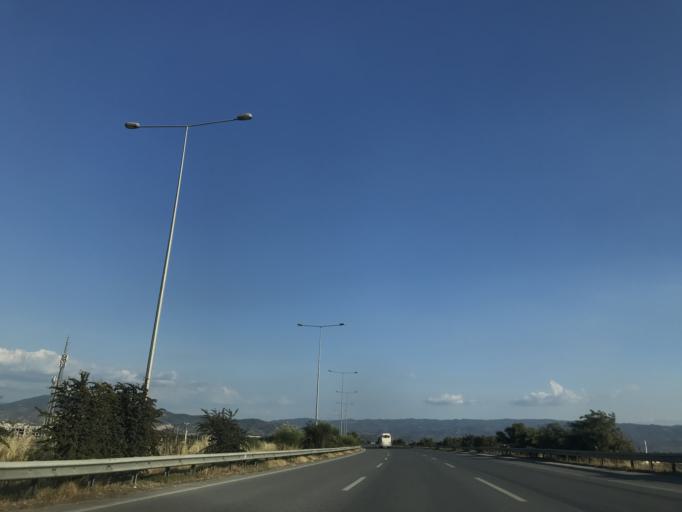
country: TR
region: Aydin
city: Aydin
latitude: 37.8309
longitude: 27.8104
